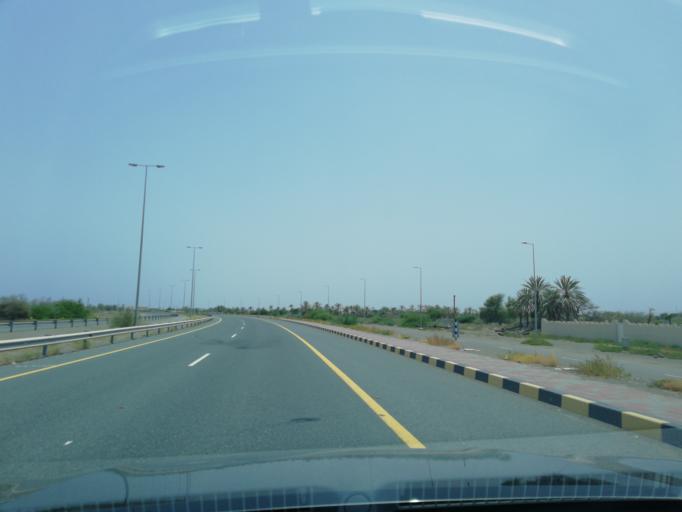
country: OM
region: Al Batinah
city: Shinas
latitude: 24.8378
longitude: 56.4259
